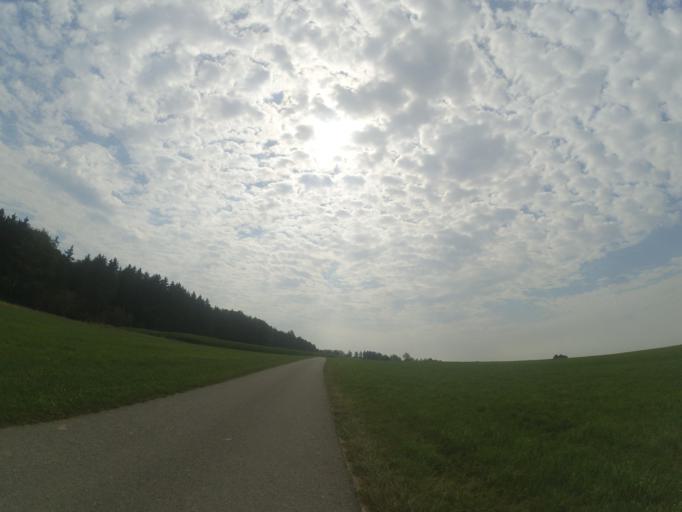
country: DE
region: Baden-Wuerttemberg
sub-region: Tuebingen Region
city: Lonsee
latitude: 48.4991
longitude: 9.8954
